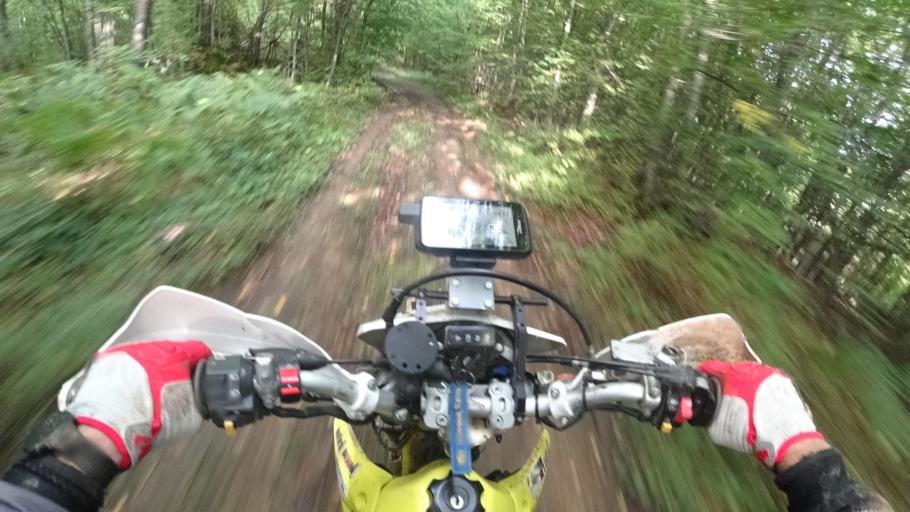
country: BA
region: Republika Srpska
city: Starcevica
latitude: 44.7173
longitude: 17.2223
